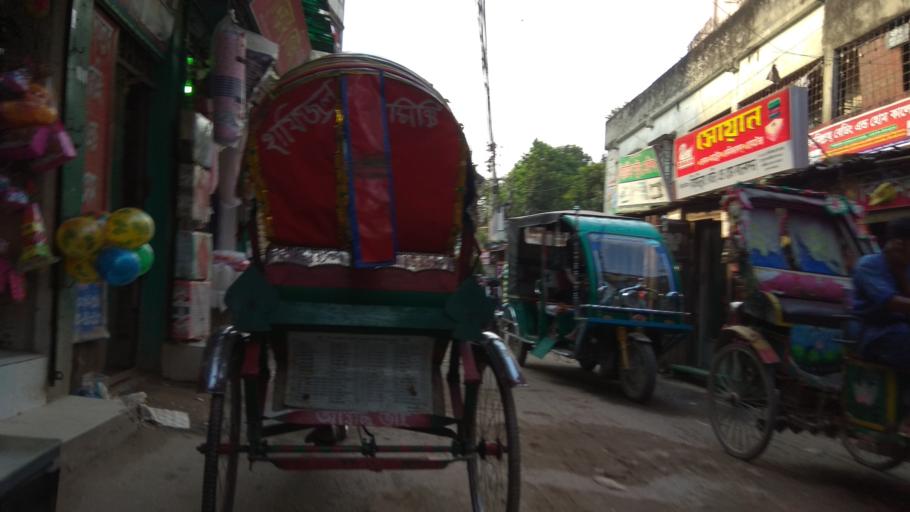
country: BD
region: Dhaka
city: Tungi
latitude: 23.8268
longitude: 90.3935
